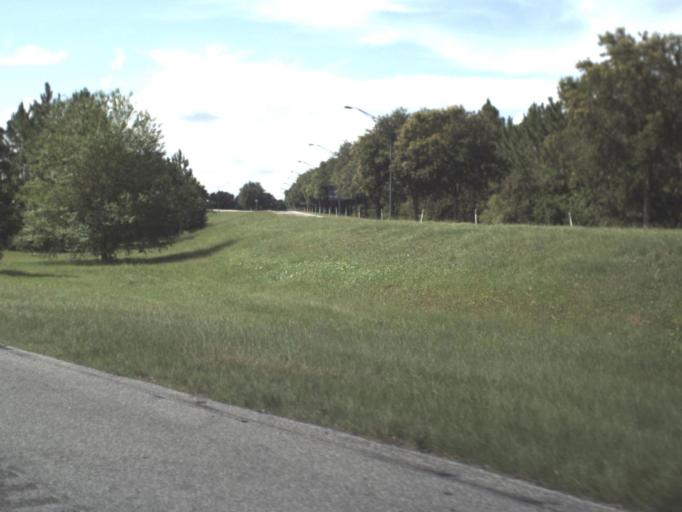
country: US
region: Florida
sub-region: Saint Johns County
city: Villano Beach
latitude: 29.9899
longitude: -81.4643
